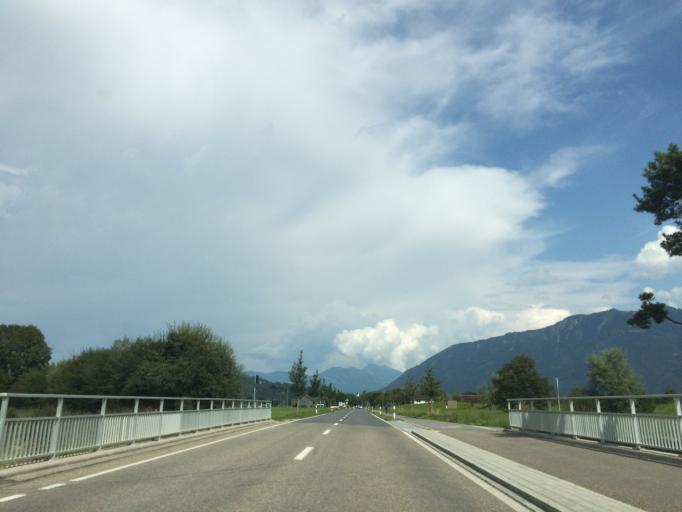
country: CH
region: Saint Gallen
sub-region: Wahlkreis Werdenberg
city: Haag (Rheintal)
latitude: 47.2072
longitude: 9.4684
